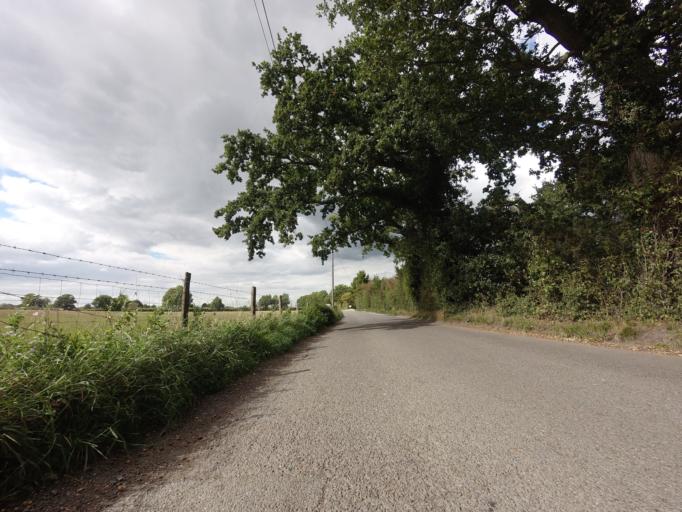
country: GB
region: England
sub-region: Kent
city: Paddock Wood
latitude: 51.1602
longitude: 0.4331
